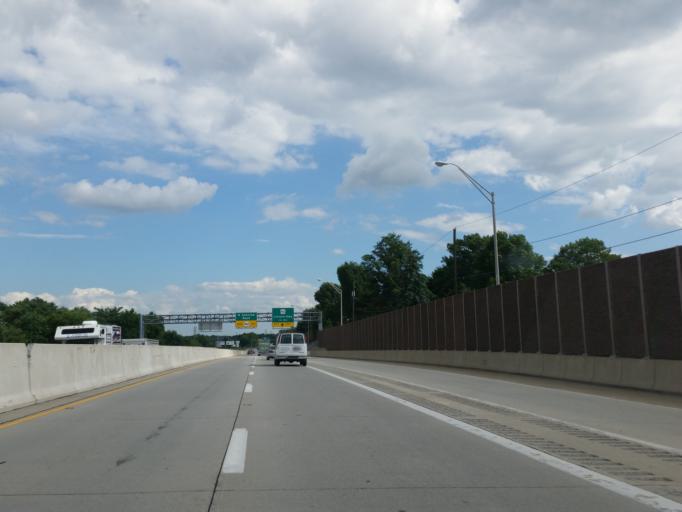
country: US
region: Pennsylvania
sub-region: Lancaster County
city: Lampeter
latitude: 40.0388
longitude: -76.2449
